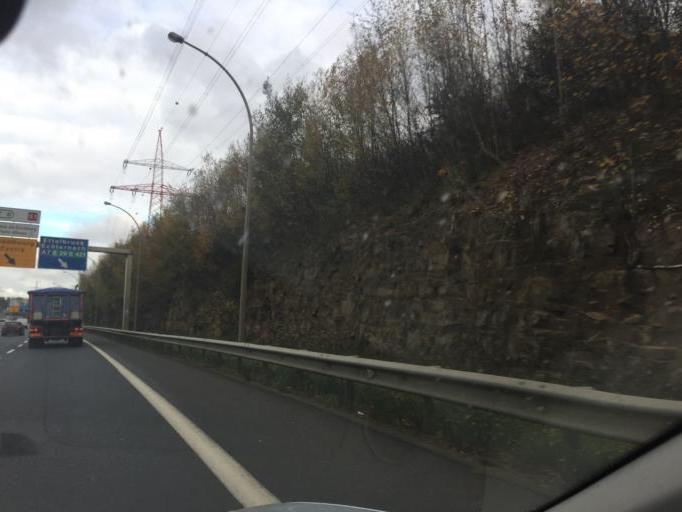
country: LU
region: Luxembourg
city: Kirchberg
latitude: 49.6287
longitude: 6.1823
